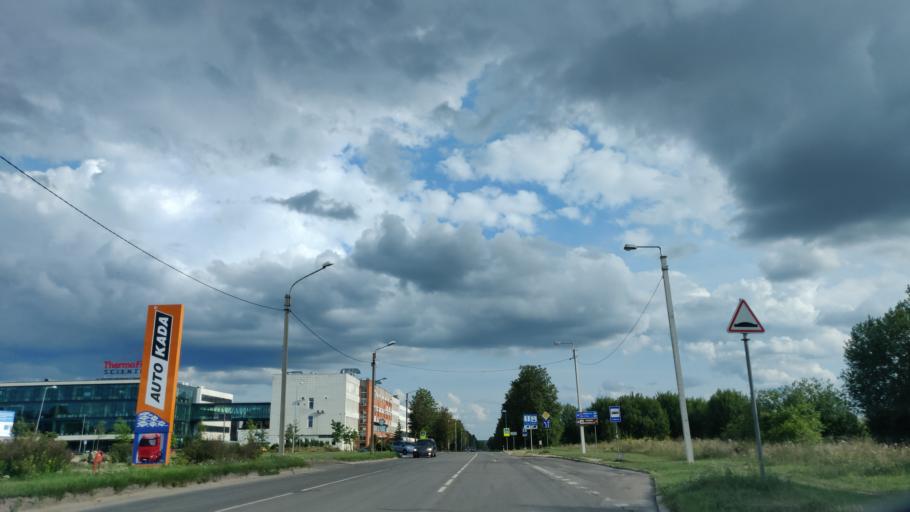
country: LT
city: Baltoji Voke
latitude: 54.6259
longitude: 25.1397
